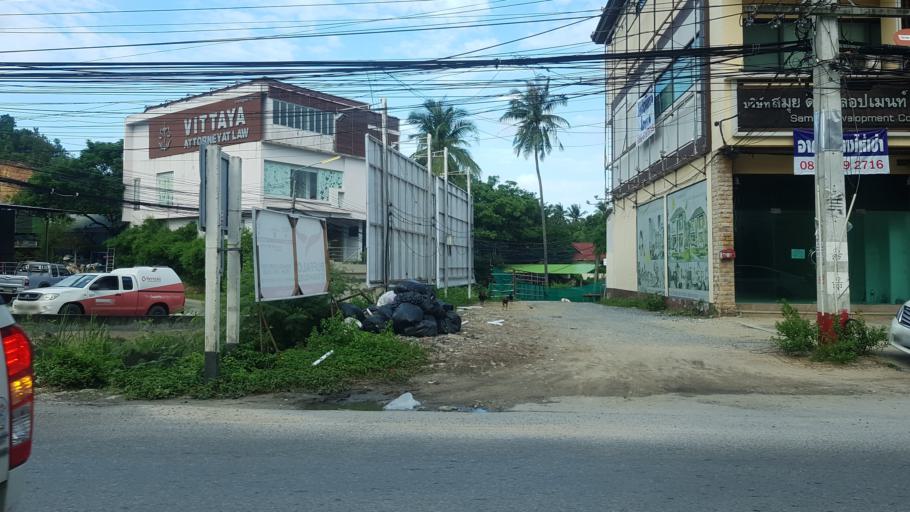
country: TH
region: Surat Thani
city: Ko Samui
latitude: 9.5357
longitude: 100.0415
